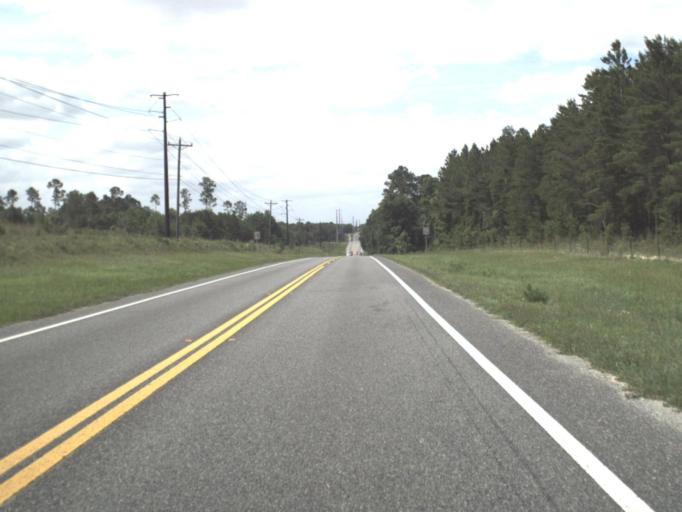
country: US
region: Florida
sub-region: Clay County
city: Middleburg
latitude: 30.0179
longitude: -81.8976
